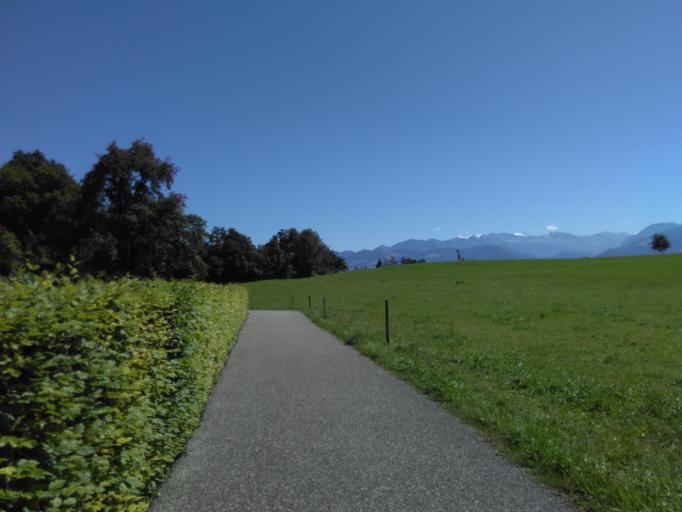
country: CH
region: Zurich
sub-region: Bezirk Hinwil
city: Rueti
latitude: 47.2543
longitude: 8.8503
